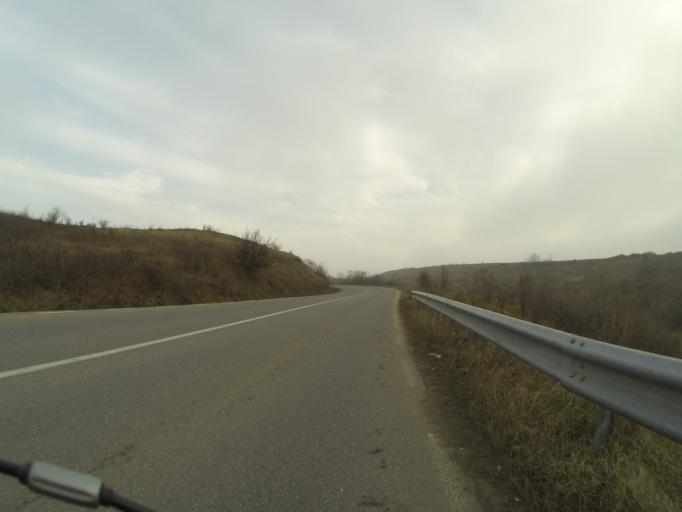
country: RO
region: Mehedinti
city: Vanju-Mare
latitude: 44.4125
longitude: 22.8792
